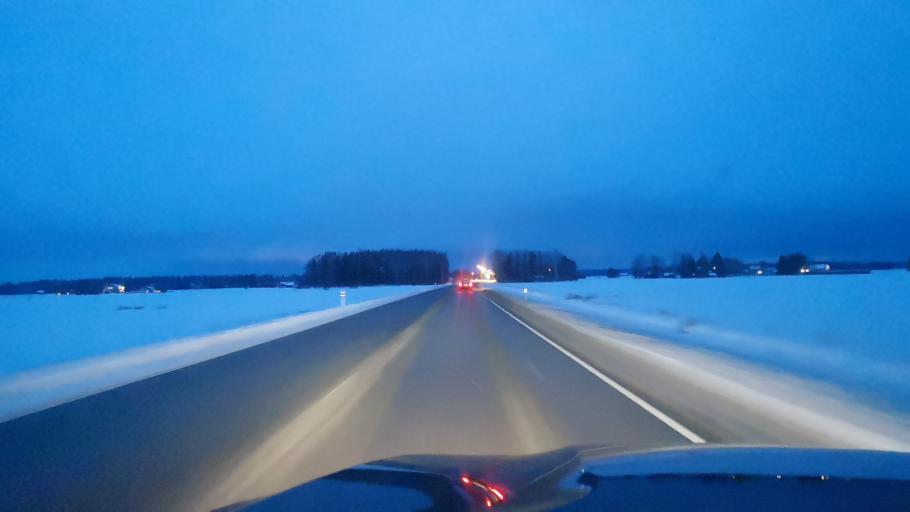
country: FI
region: Varsinais-Suomi
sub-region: Loimaa
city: Loimaa
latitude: 60.8806
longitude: 23.0791
